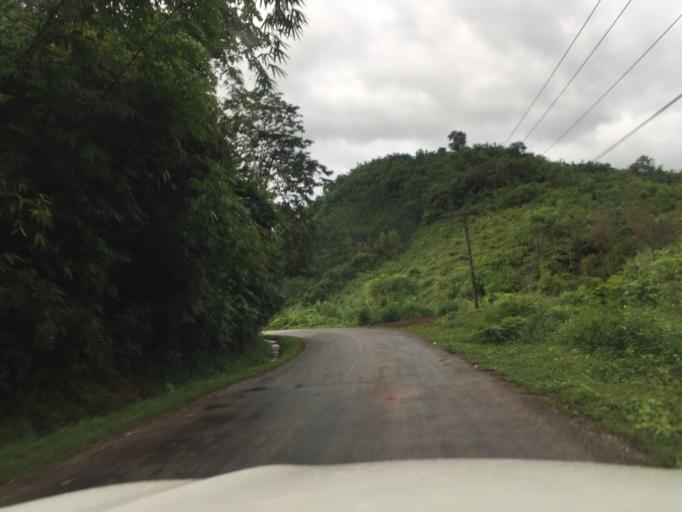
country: LA
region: Oudomxai
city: Muang La
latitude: 20.7972
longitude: 102.0857
